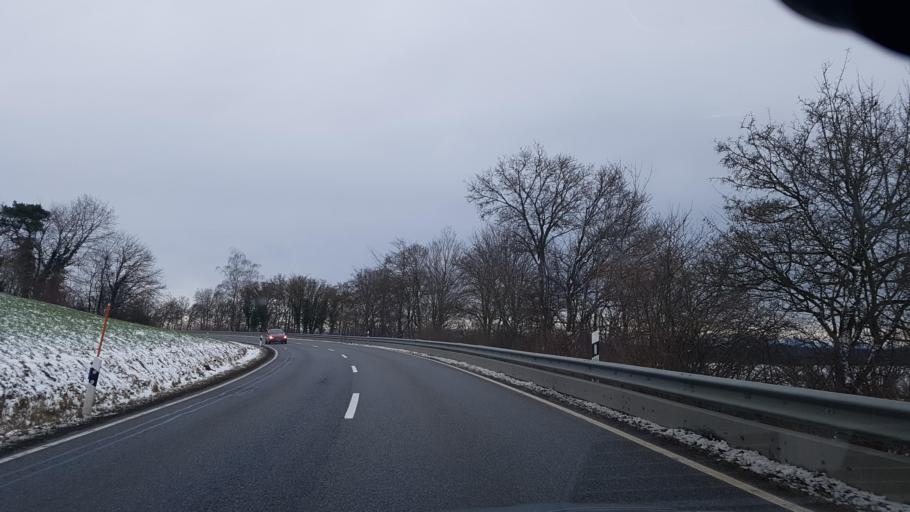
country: DE
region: Bavaria
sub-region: Upper Bavaria
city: Haag in Oberbayern
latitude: 48.1824
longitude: 12.1511
